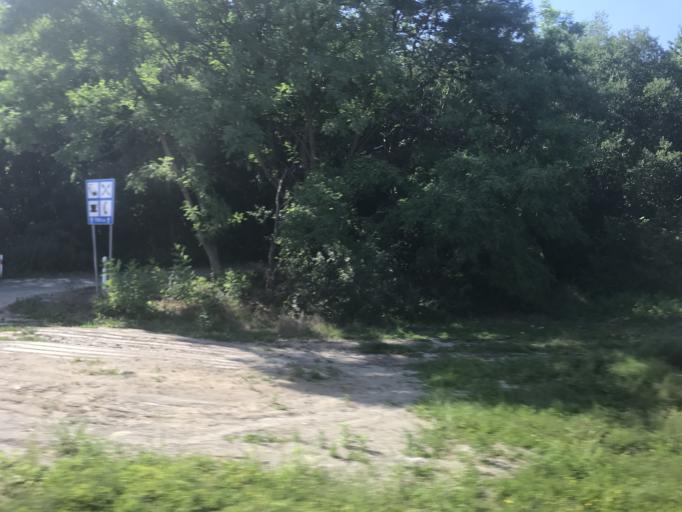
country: PL
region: West Pomeranian Voivodeship
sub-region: Powiat policki
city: Kolbaskowo
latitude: 53.3427
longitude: 14.4392
